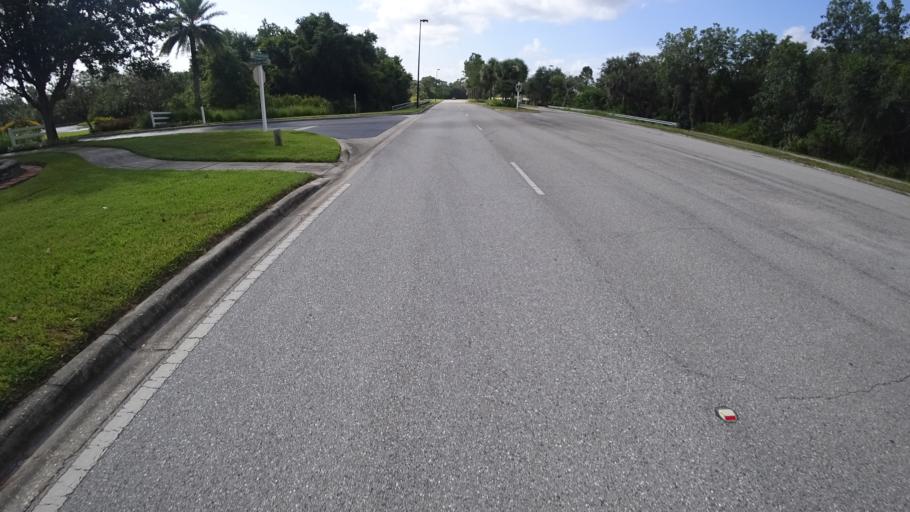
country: US
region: Florida
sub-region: Sarasota County
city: The Meadows
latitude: 27.4023
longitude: -82.4491
